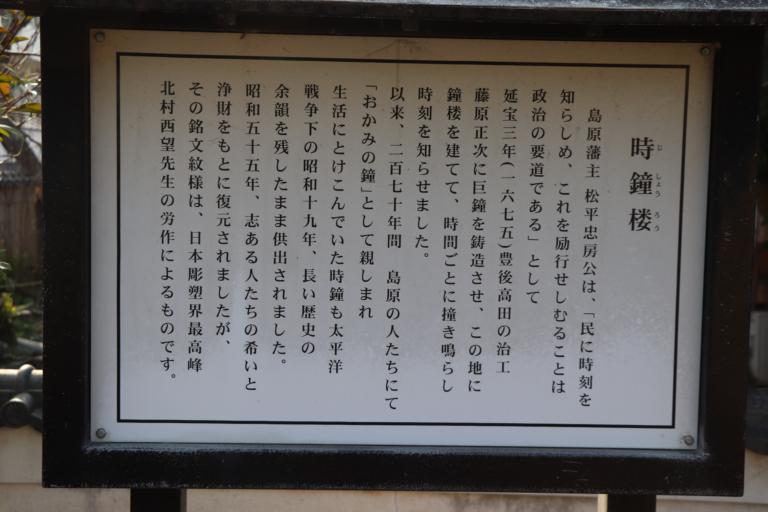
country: JP
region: Nagasaki
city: Shimabara
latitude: 32.7914
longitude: 130.3648
